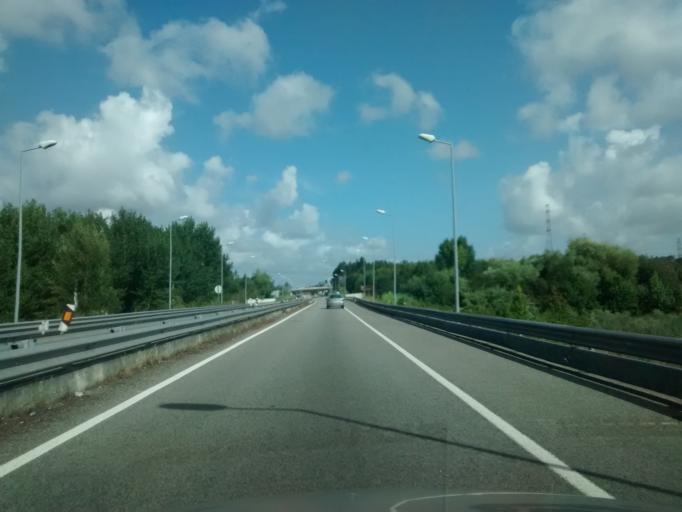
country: PT
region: Aveiro
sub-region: Anadia
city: Arcos
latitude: 40.4622
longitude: -8.4603
